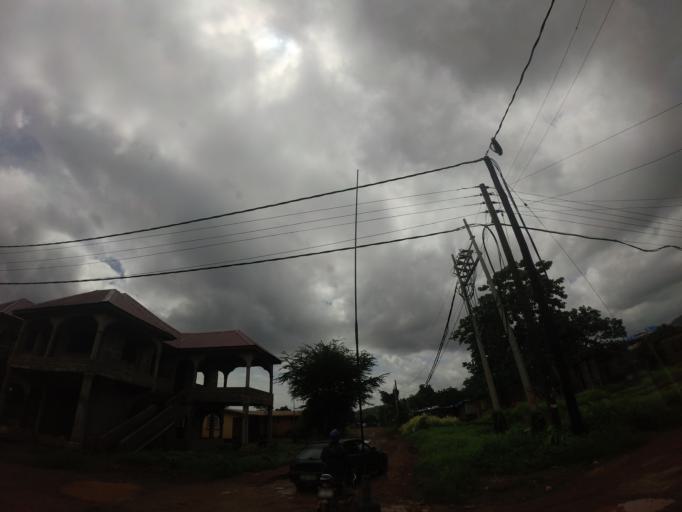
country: SL
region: Western Area
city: Hastings
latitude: 8.3805
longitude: -13.1356
